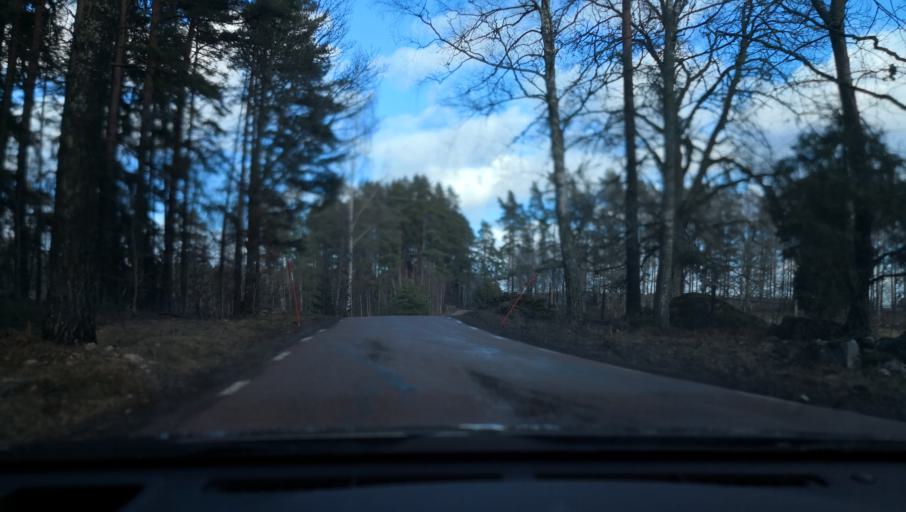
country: SE
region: Vaestmanland
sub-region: Arboga Kommun
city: Arboga
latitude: 59.3164
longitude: 15.7677
